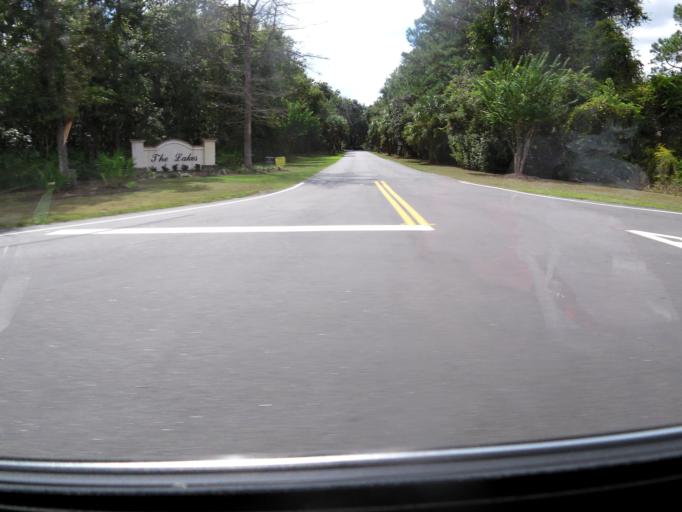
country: US
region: Georgia
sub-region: Glynn County
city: Dock Junction
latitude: 31.1560
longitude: -81.5919
